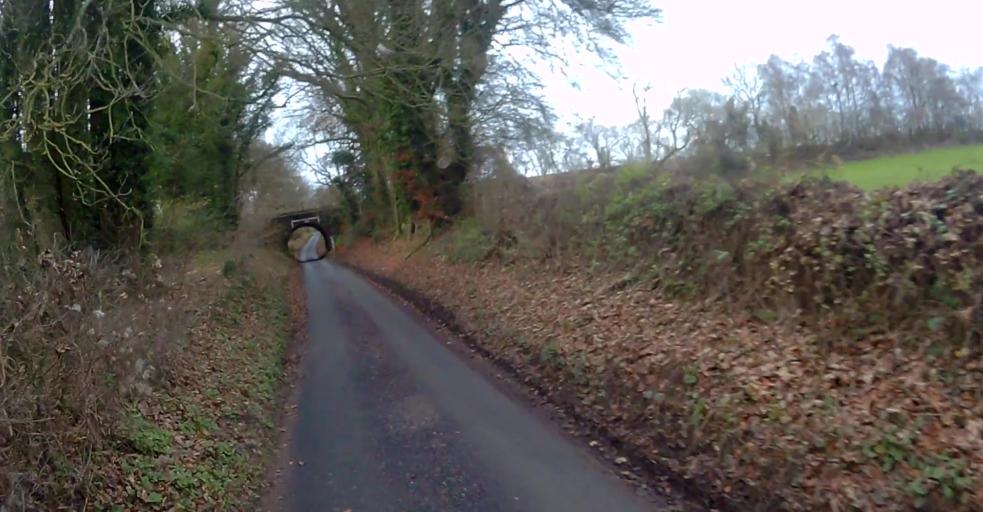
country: GB
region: England
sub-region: Hampshire
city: Overton
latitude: 51.2242
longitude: -1.2323
